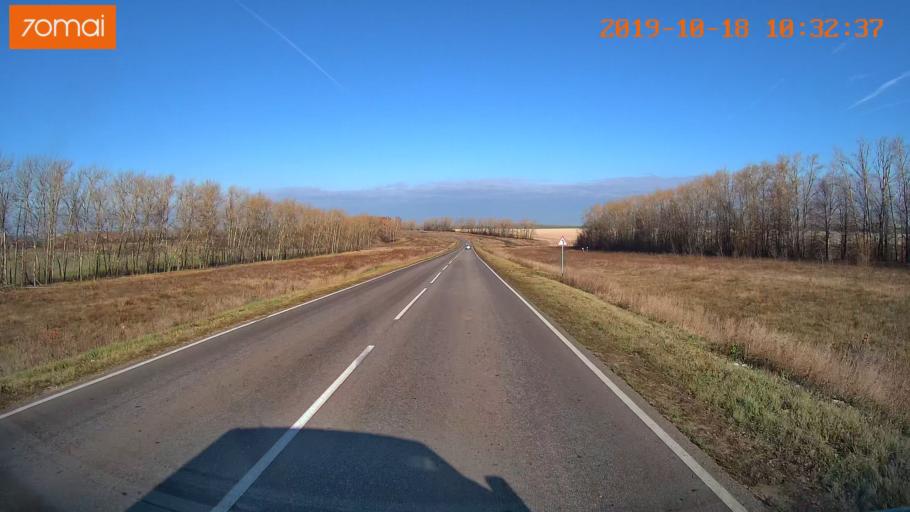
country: RU
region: Tula
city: Kurkino
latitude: 53.4965
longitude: 38.6211
